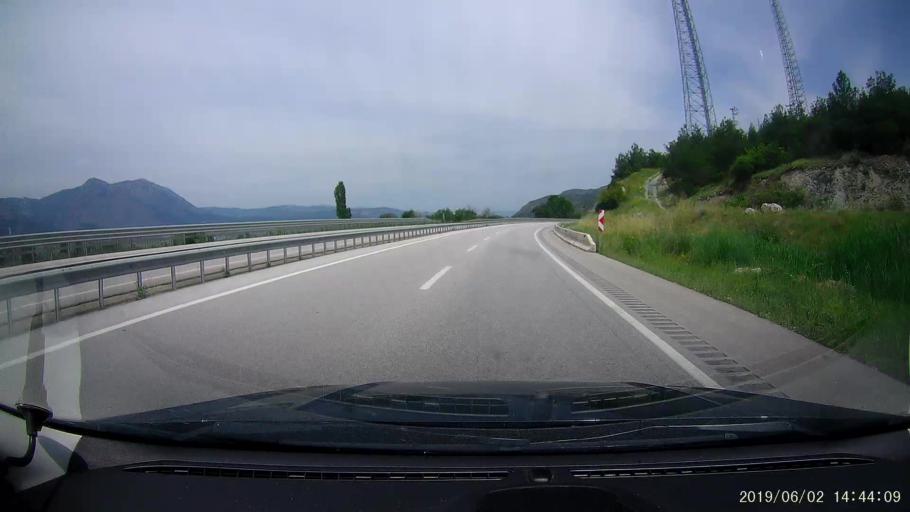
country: TR
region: Corum
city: Hacihamza
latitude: 41.1020
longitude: 34.4071
